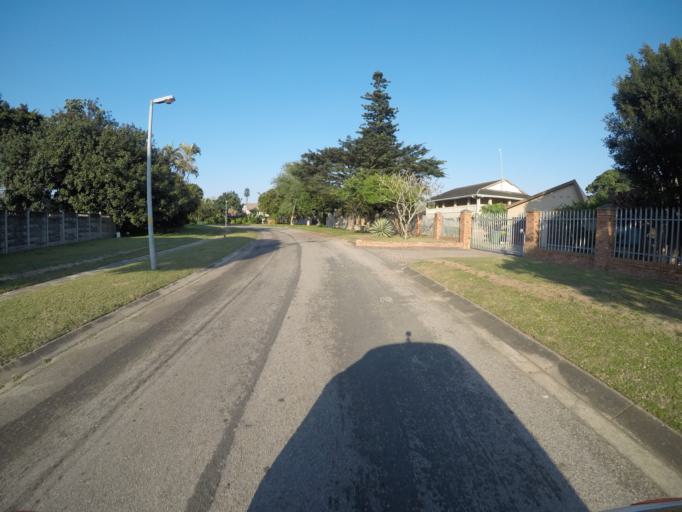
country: ZA
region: KwaZulu-Natal
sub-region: uThungulu District Municipality
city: Richards Bay
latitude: -28.7756
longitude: 32.1020
